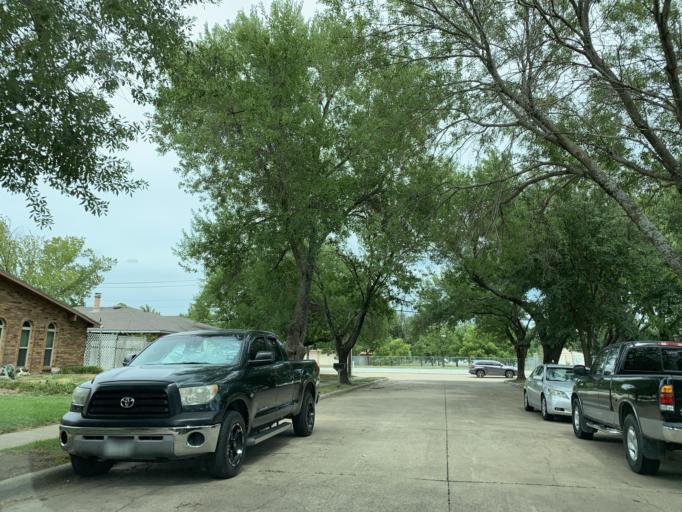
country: US
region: Texas
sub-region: Dallas County
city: Cedar Hill
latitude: 32.6498
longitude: -97.0286
